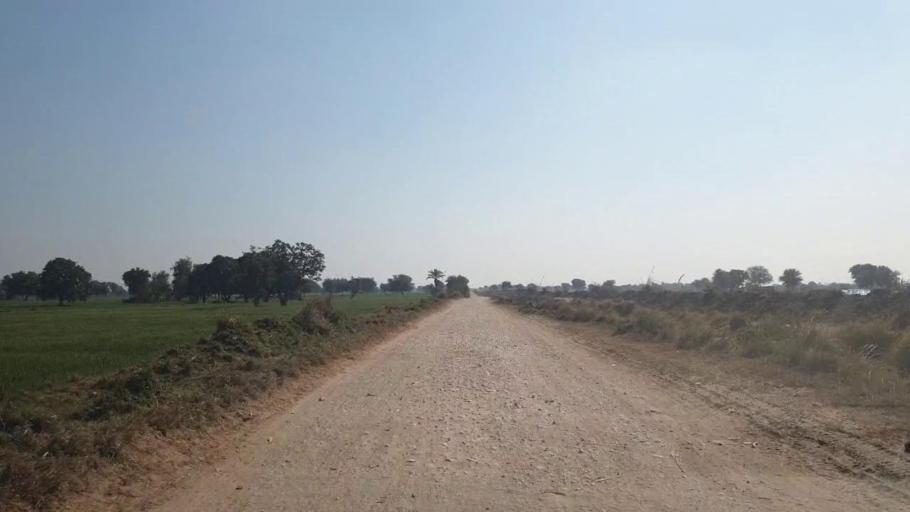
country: PK
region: Sindh
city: Shahdadpur
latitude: 25.9640
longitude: 68.6201
